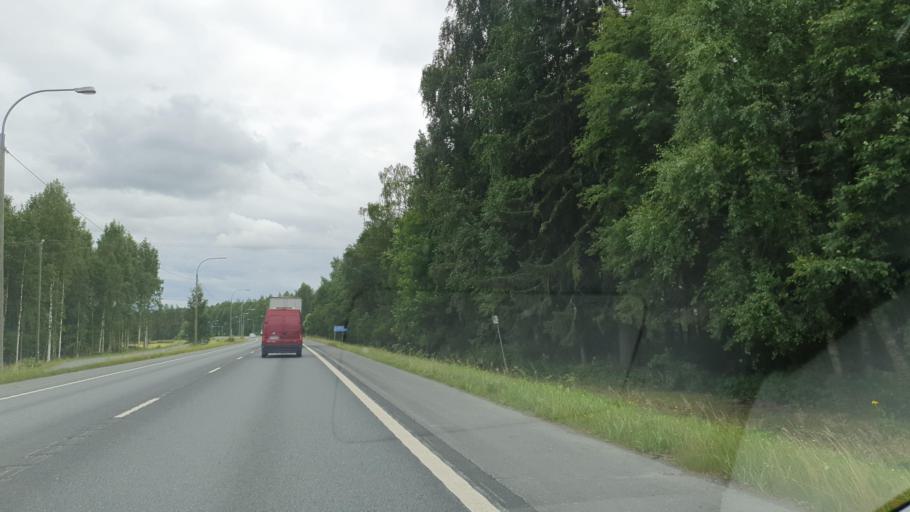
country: FI
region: Northern Savo
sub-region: Ylae-Savo
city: Iisalmi
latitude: 63.4971
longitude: 27.2681
